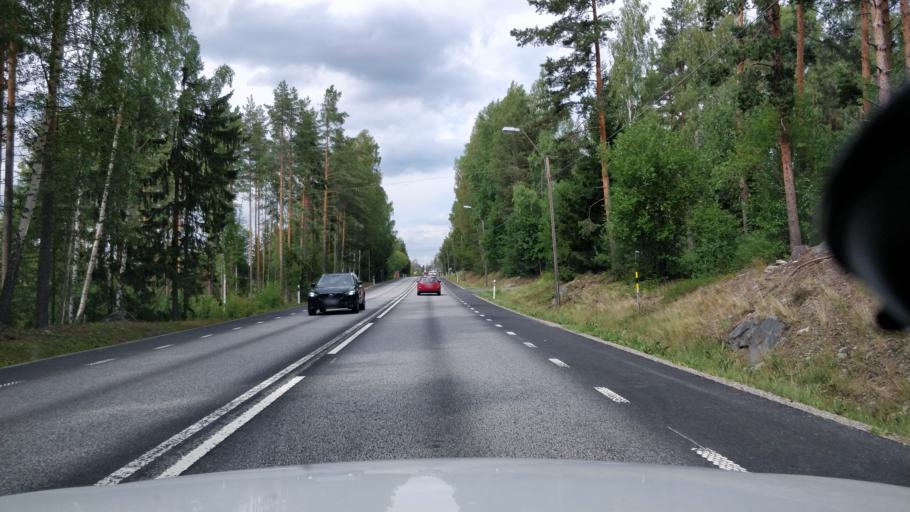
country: SE
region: Dalarna
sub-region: Faluns Kommun
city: Grycksbo
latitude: 60.6916
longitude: 15.4877
